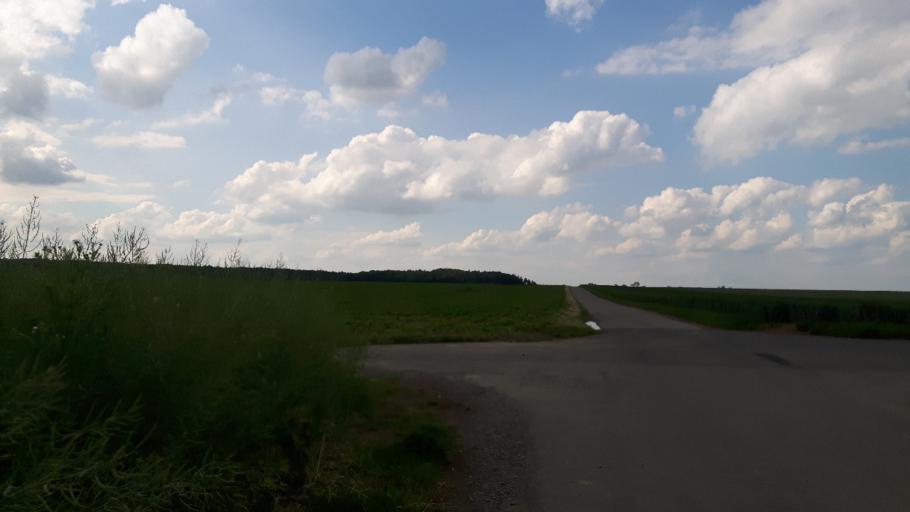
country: DE
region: Bavaria
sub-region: Regierungsbezirk Unterfranken
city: Geroldshausen
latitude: 49.6976
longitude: 9.8967
